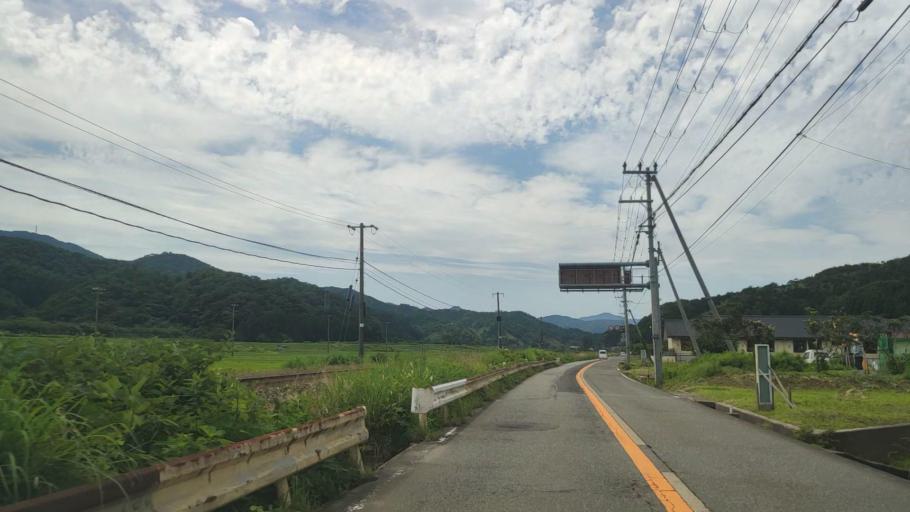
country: JP
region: Hyogo
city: Toyooka
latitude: 35.6415
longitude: 134.7581
